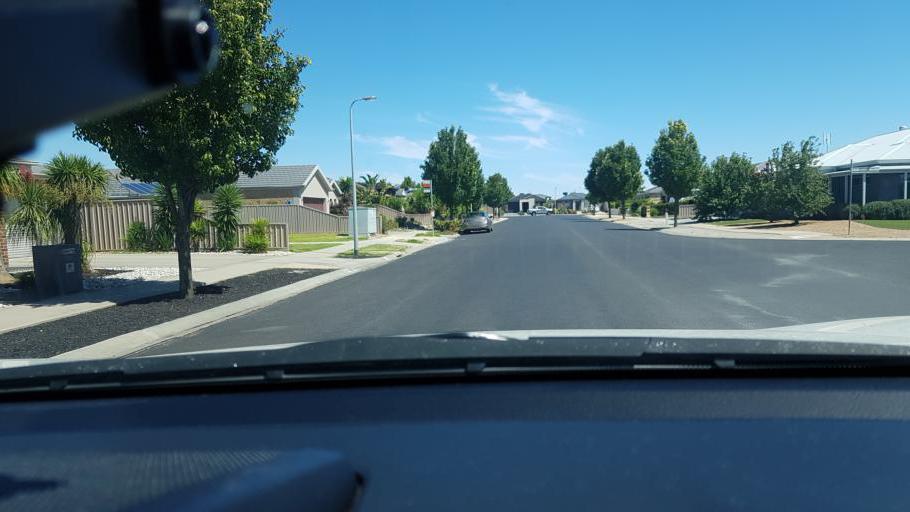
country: AU
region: Victoria
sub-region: Horsham
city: Horsham
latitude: -36.7122
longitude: 142.1807
